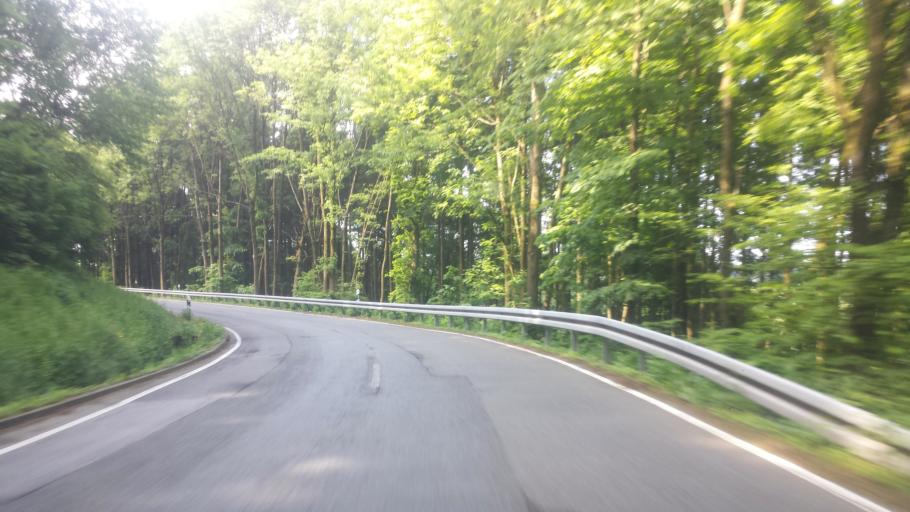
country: DE
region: Hesse
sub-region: Regierungsbezirk Darmstadt
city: Wald-Michelbach
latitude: 49.5671
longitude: 8.8058
